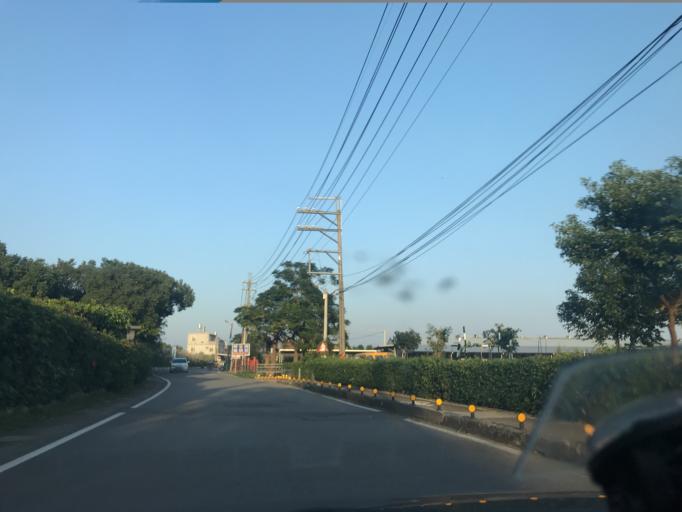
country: TW
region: Taiwan
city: Daxi
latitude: 24.8450
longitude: 121.2223
